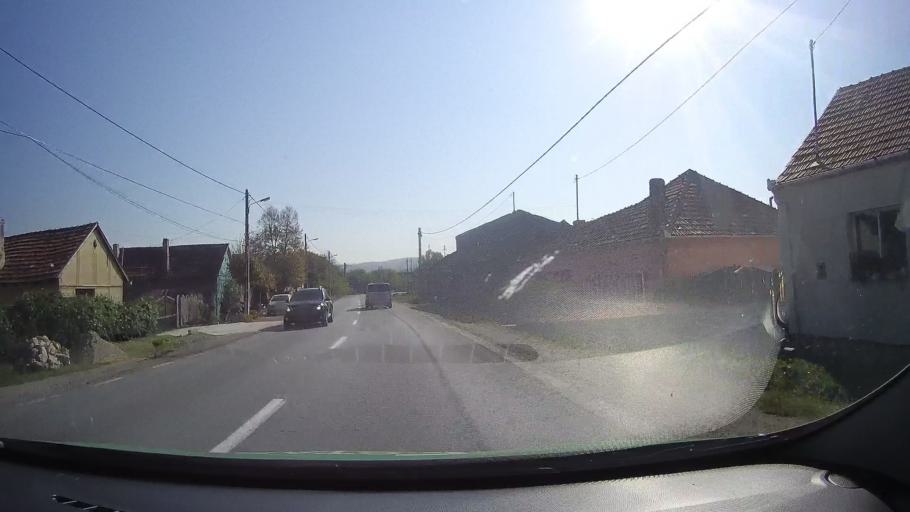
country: RO
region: Hunedoara
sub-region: Comuna Dobra
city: Dobra
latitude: 45.9177
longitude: 22.5593
